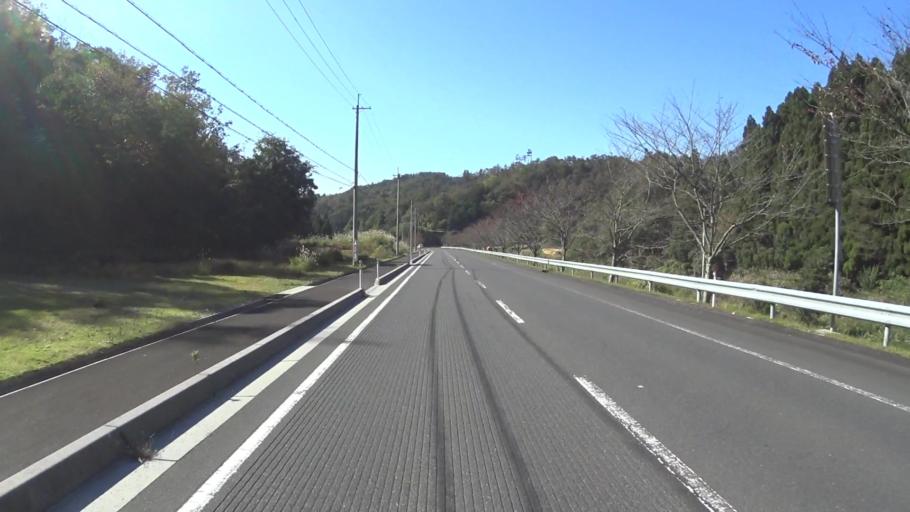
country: JP
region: Hyogo
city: Toyooka
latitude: 35.5758
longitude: 134.9932
